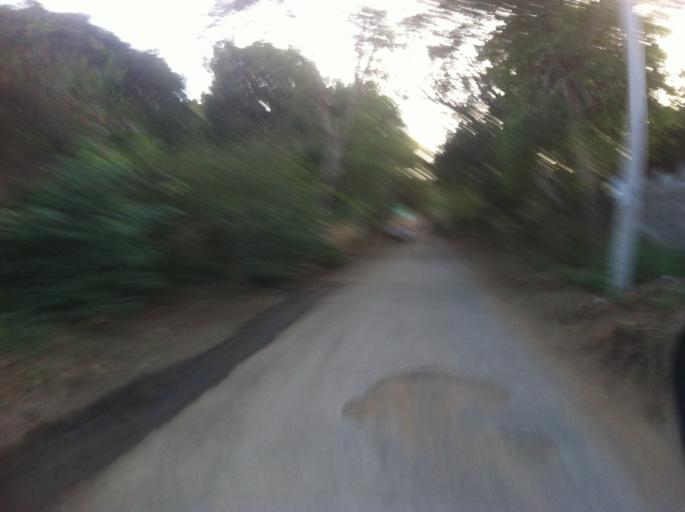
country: NI
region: Managua
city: Ciudad Sandino
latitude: 12.1048
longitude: -86.3289
